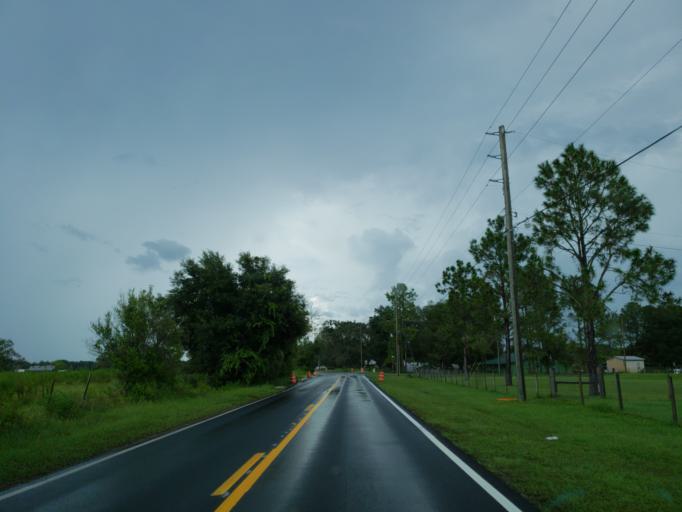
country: US
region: Florida
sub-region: Pasco County
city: Land O' Lakes
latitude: 28.2926
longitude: -82.4324
